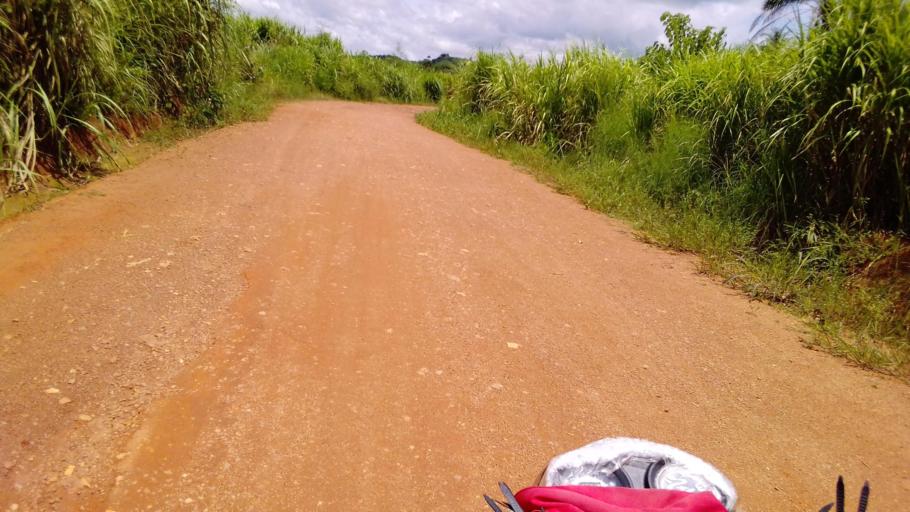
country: SL
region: Eastern Province
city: Koidu
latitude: 8.6722
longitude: -10.9398
